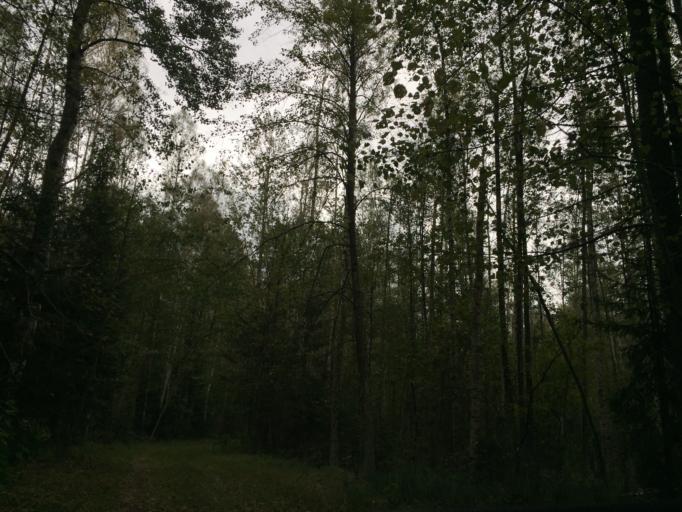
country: LV
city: Tireli
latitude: 56.8921
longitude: 23.5522
